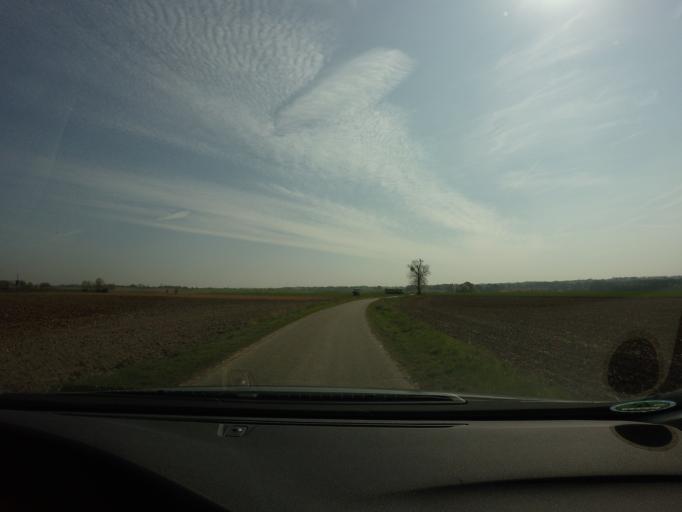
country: NL
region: Limburg
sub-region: Valkenburg aan de Geul
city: Berg
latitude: 50.8374
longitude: 5.7941
